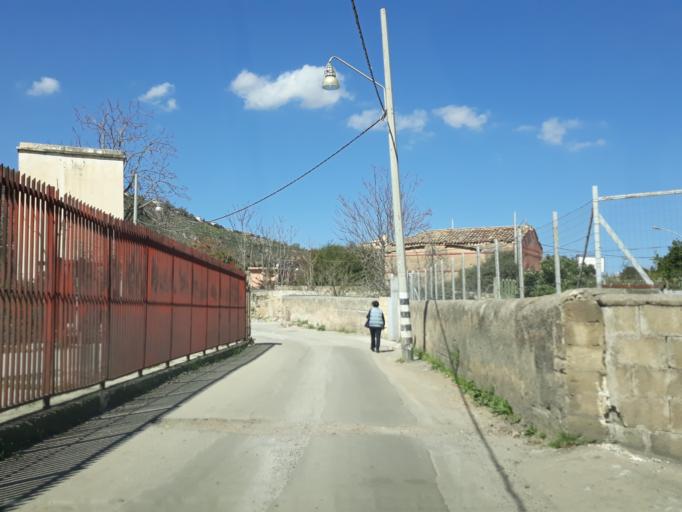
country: IT
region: Sicily
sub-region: Palermo
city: Villa Ciambra
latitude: 38.0903
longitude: 13.3213
